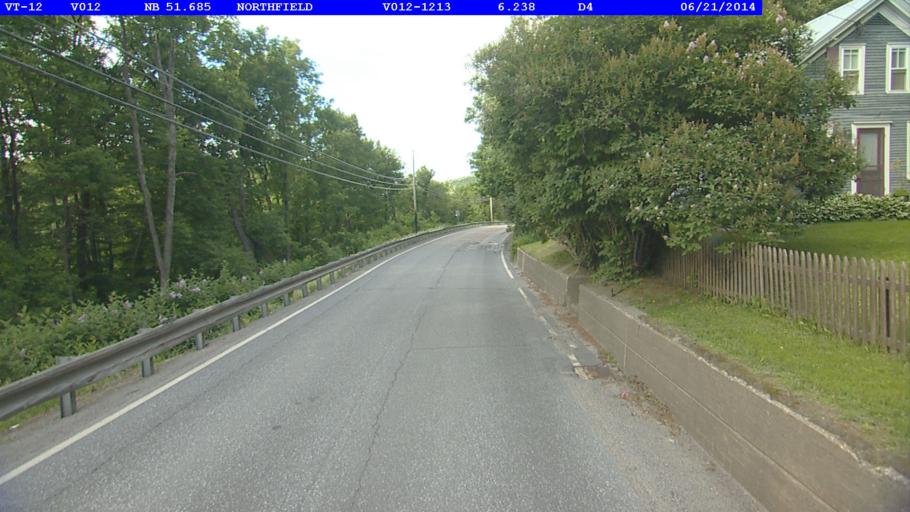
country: US
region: Vermont
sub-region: Washington County
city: Northfield
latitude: 44.1750
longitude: -72.6448
